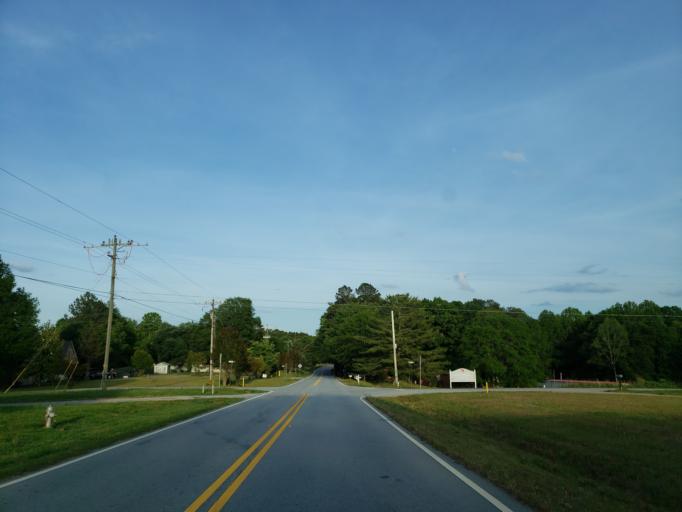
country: US
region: Georgia
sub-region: Carroll County
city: Mount Zion
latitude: 33.6086
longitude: -85.1506
